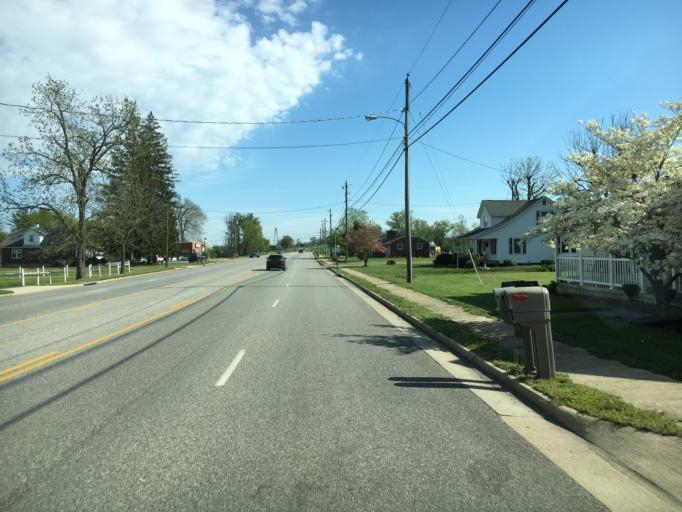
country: US
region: Virginia
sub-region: Augusta County
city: Dooms
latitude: 38.1099
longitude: -78.8572
